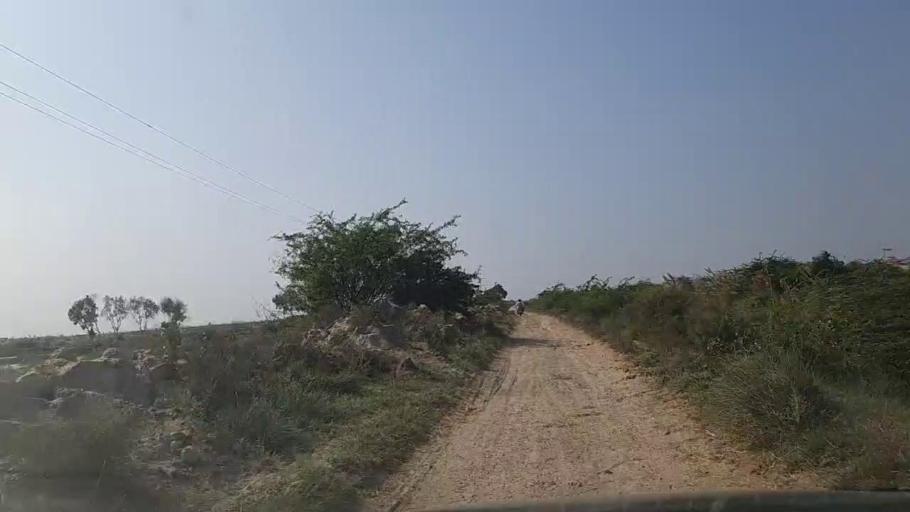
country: PK
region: Sindh
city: Gharo
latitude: 24.7212
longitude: 67.6667
